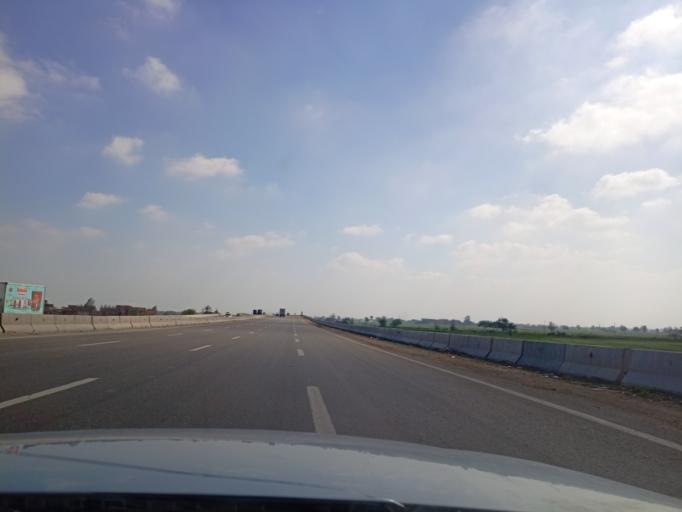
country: EG
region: Eastern Province
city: Mashtul as Suq
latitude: 30.4543
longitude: 31.4007
